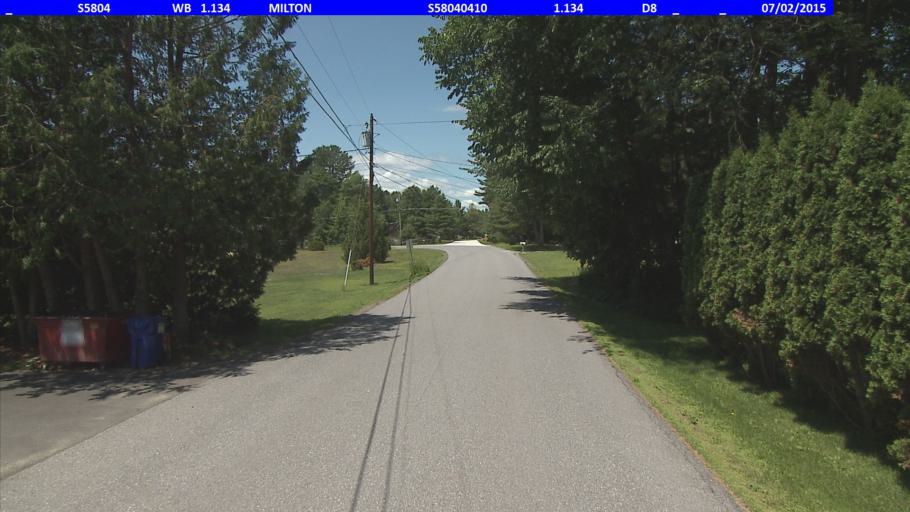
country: US
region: Vermont
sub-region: Chittenden County
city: Milton
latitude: 44.6571
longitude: -73.1514
